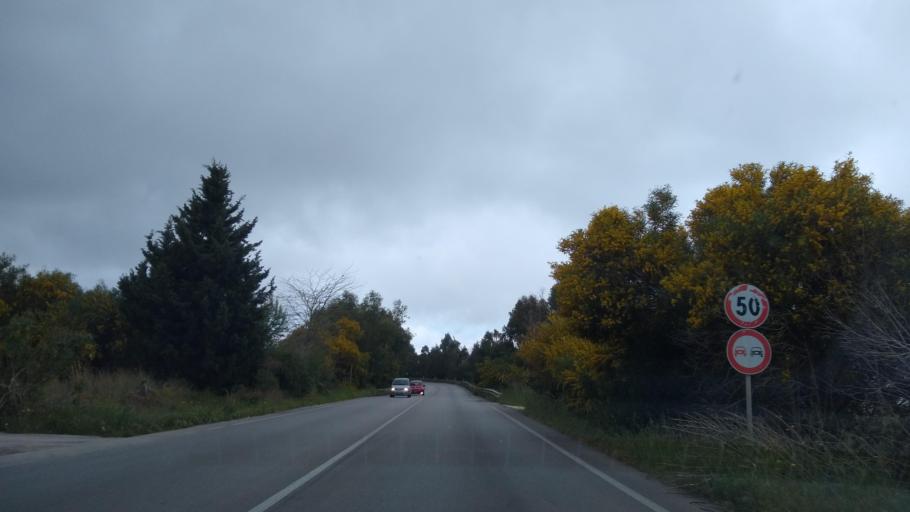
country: IT
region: Sicily
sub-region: Trapani
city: Alcamo
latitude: 37.9917
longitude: 12.9568
